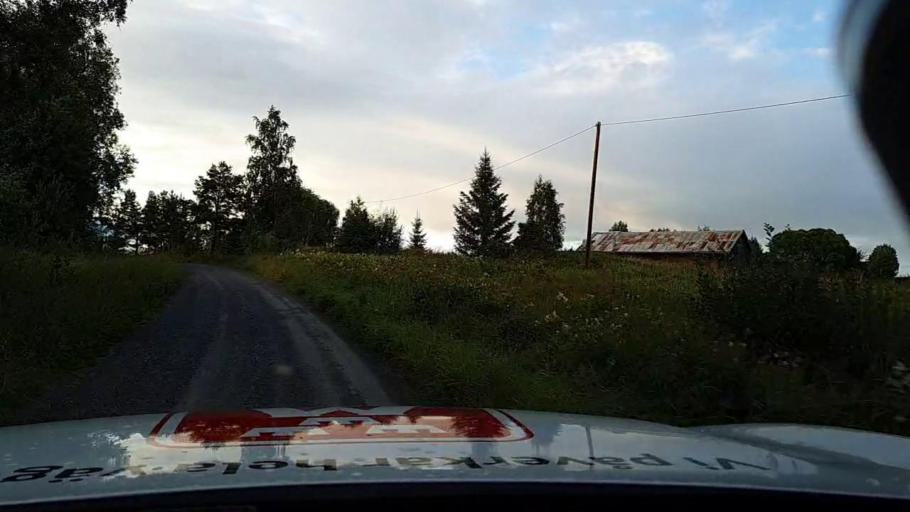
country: SE
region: Jaemtland
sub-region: Bergs Kommun
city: Hoverberg
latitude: 62.8708
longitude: 14.6221
